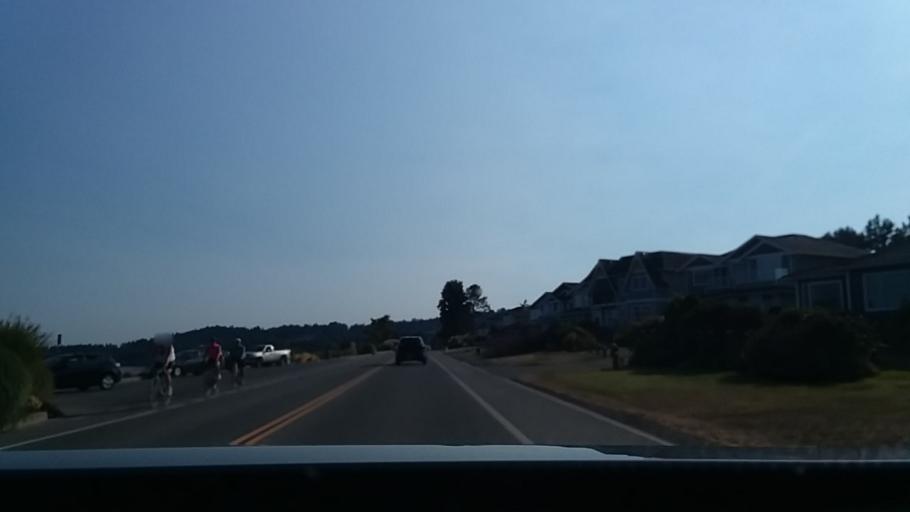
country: CA
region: British Columbia
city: North Saanich
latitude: 48.6404
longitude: -123.4014
